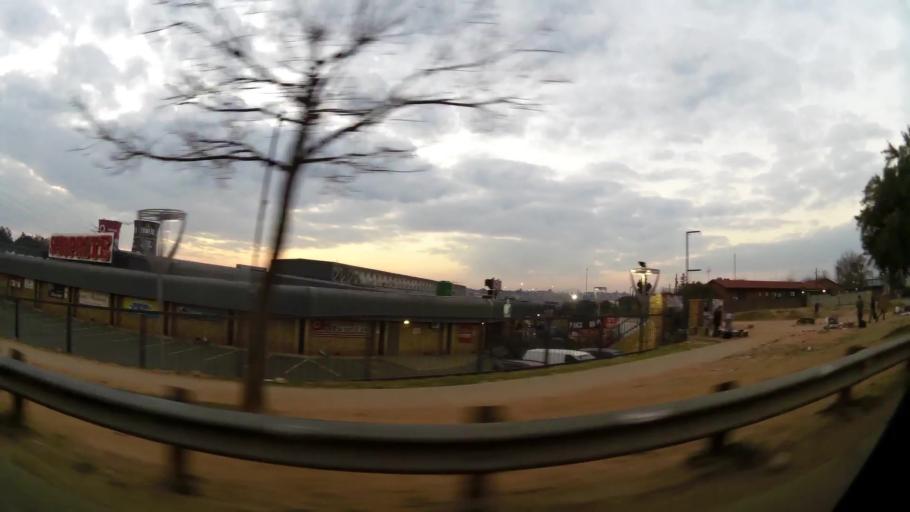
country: ZA
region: Gauteng
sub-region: City of Johannesburg Metropolitan Municipality
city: Soweto
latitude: -26.2589
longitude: 27.9314
